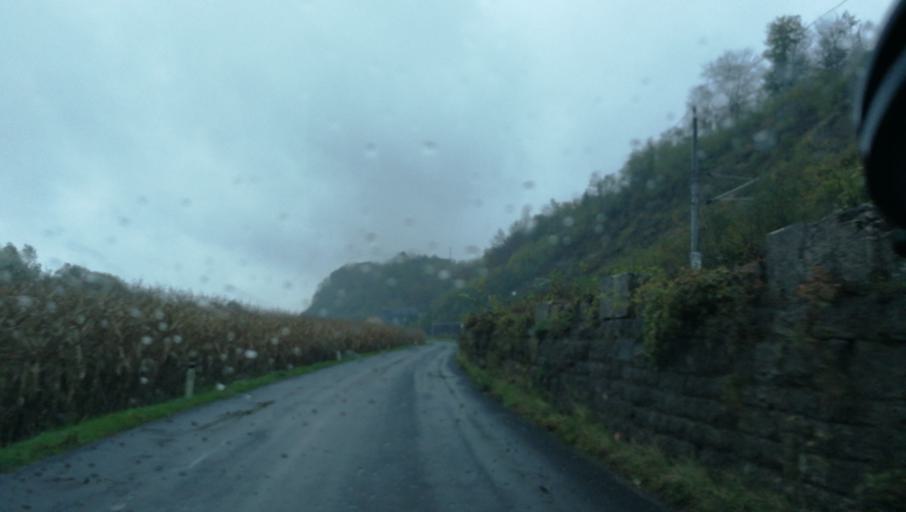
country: AT
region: Styria
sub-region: Politischer Bezirk Leibnitz
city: Ehrenhausen
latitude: 46.7237
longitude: 15.6006
